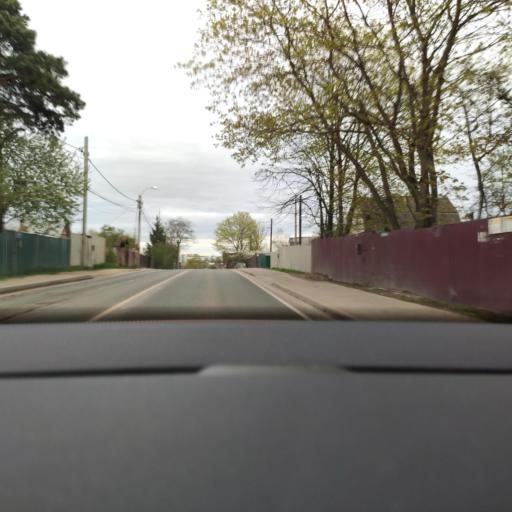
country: RU
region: Moskovskaya
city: Skhodnya
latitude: 55.9908
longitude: 37.3256
